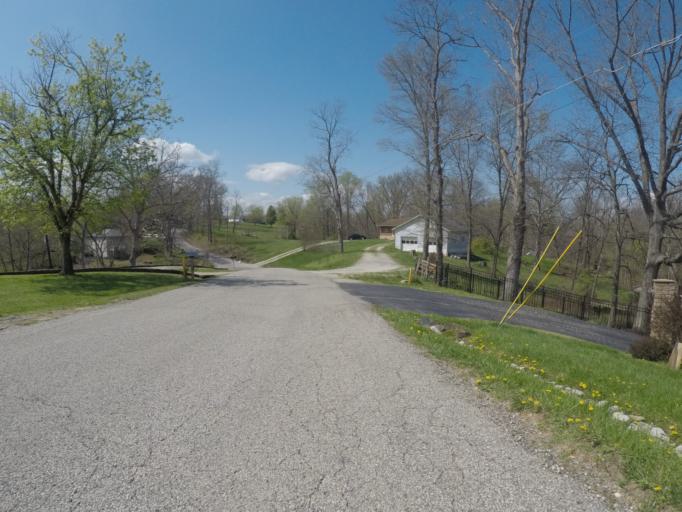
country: US
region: Ohio
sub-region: Lawrence County
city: Burlington
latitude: 38.3864
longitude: -82.5364
